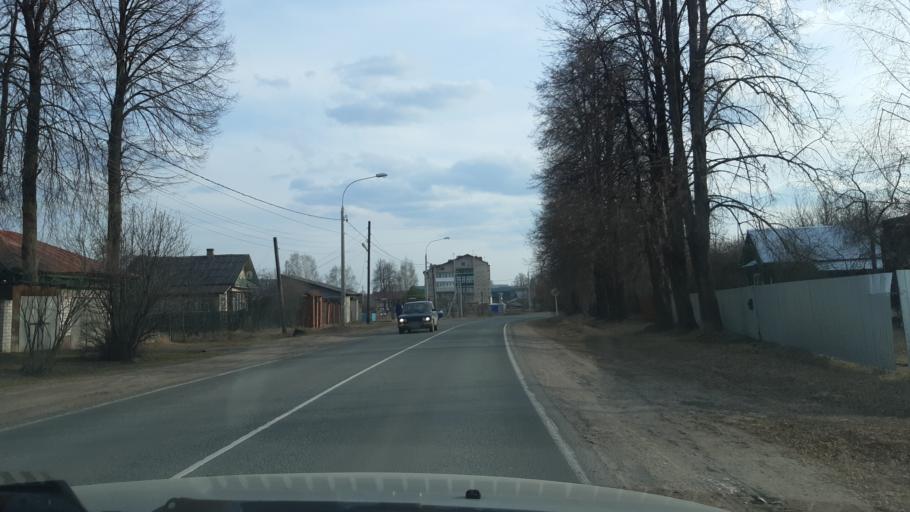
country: RU
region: Vladimir
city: Nikologory
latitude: 56.1507
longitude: 41.9958
